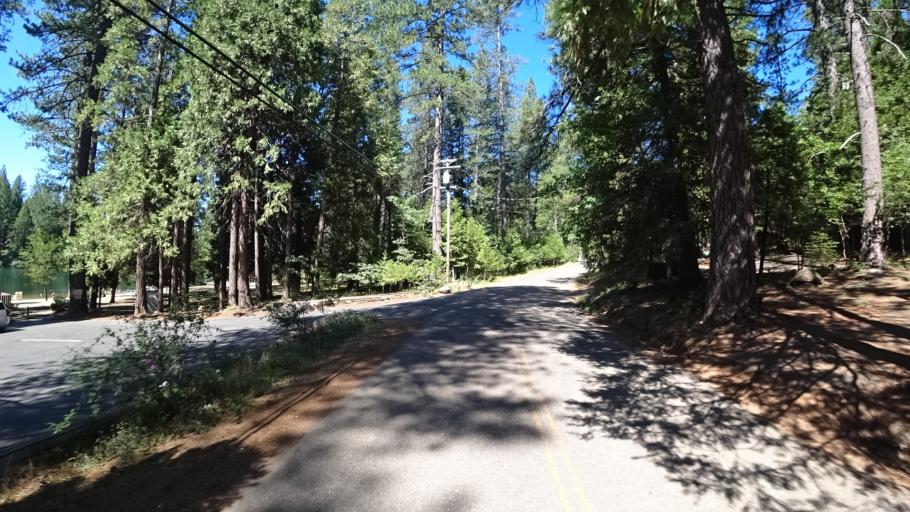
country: US
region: California
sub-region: Calaveras County
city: Arnold
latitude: 38.2356
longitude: -120.3742
